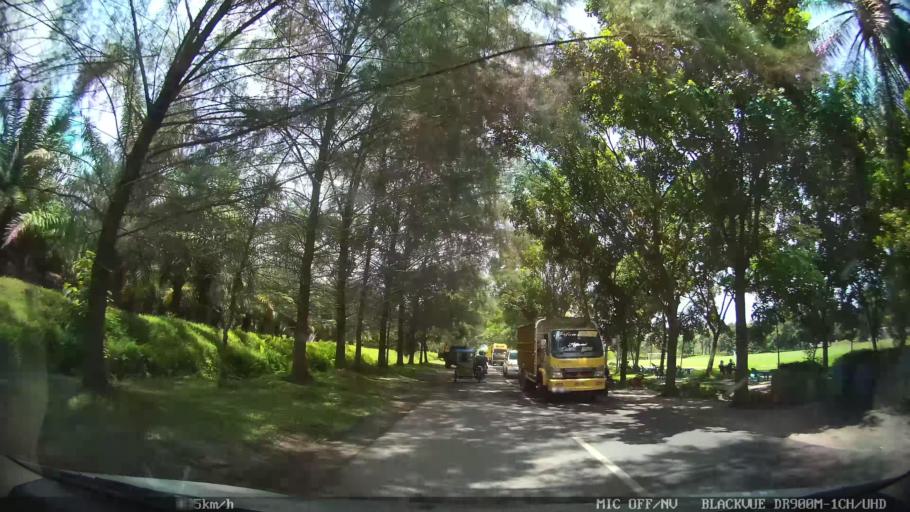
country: ID
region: North Sumatra
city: Percut
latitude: 3.5419
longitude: 98.8711
